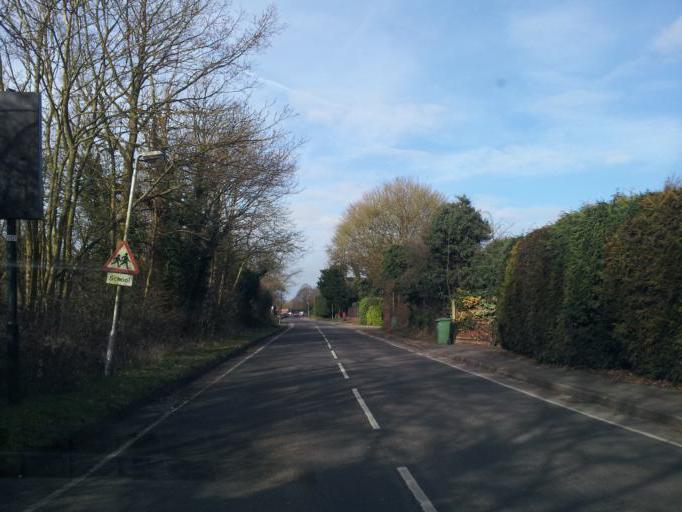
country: GB
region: England
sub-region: Hertfordshire
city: St Albans
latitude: 51.7477
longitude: -0.2844
